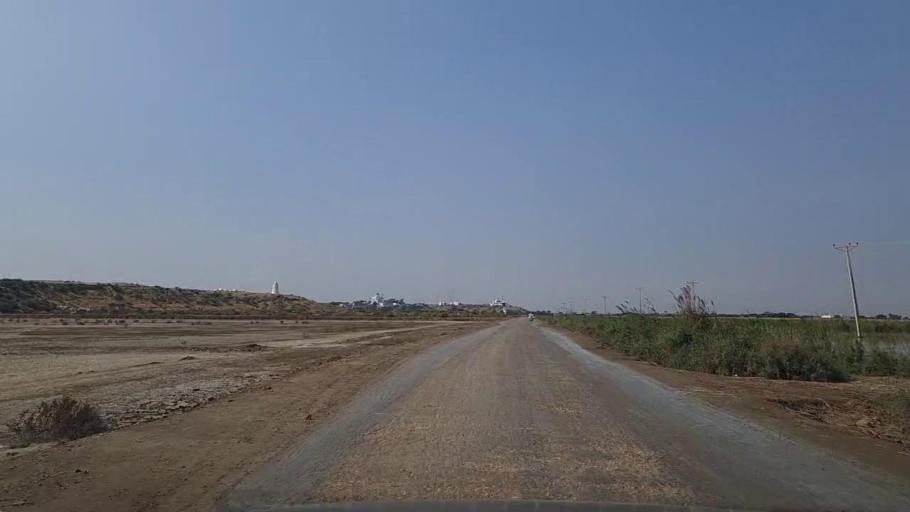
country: PK
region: Sindh
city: Chuhar Jamali
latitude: 24.5528
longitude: 67.8912
